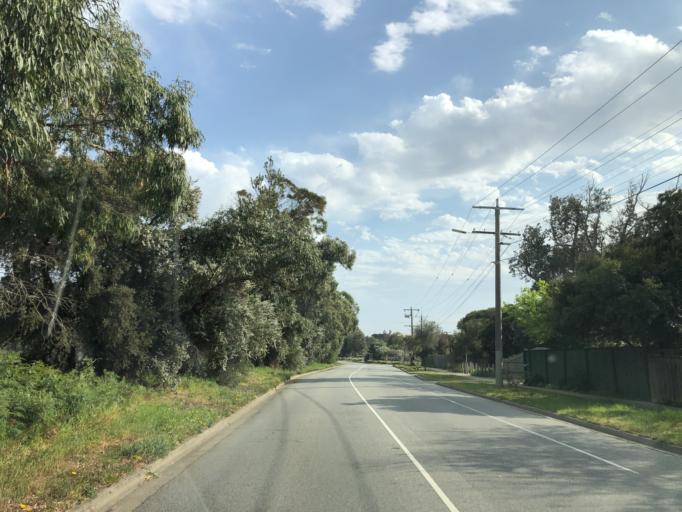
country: AU
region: Victoria
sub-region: Kingston
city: Carrum
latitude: -38.0909
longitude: 145.1283
